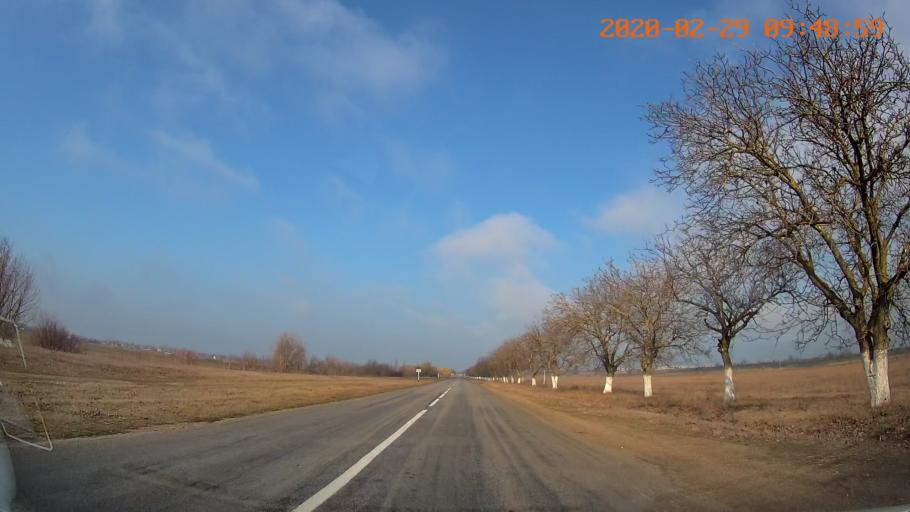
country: MD
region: Telenesti
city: Crasnoe
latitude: 46.6939
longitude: 29.7792
